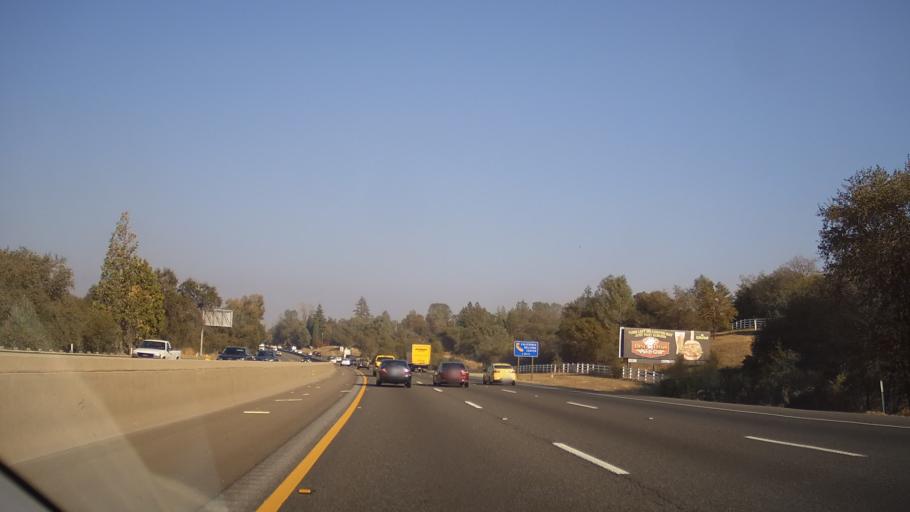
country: US
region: California
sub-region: Placer County
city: Newcastle
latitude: 38.8818
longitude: -121.1066
